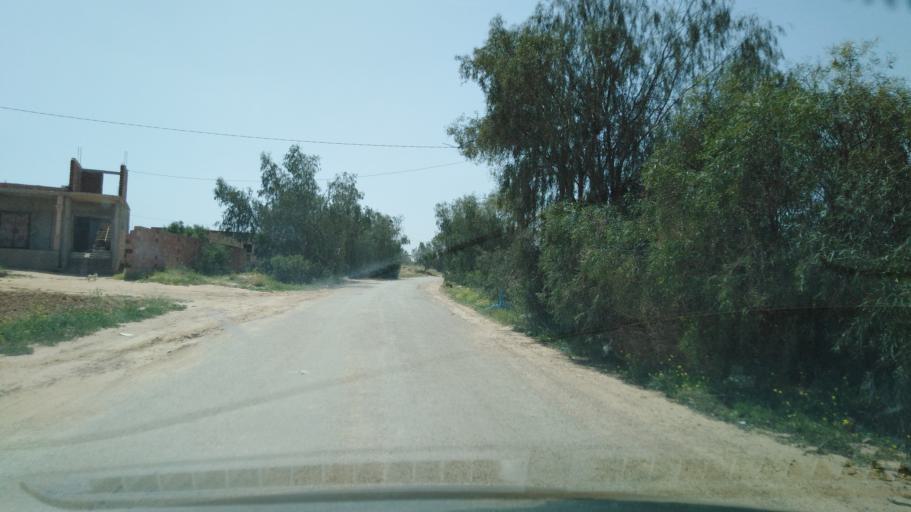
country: TN
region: Safaqis
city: Sfax
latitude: 34.7229
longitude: 10.5302
